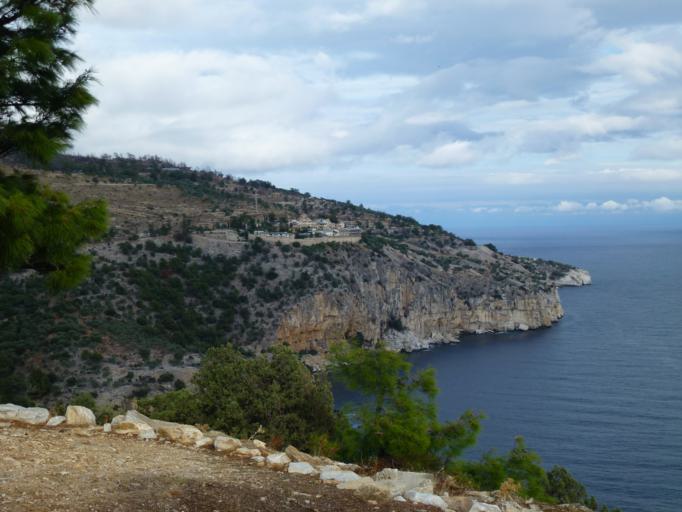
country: GR
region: East Macedonia and Thrace
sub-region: Nomos Kavalas
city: Limenaria
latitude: 40.5937
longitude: 24.6902
